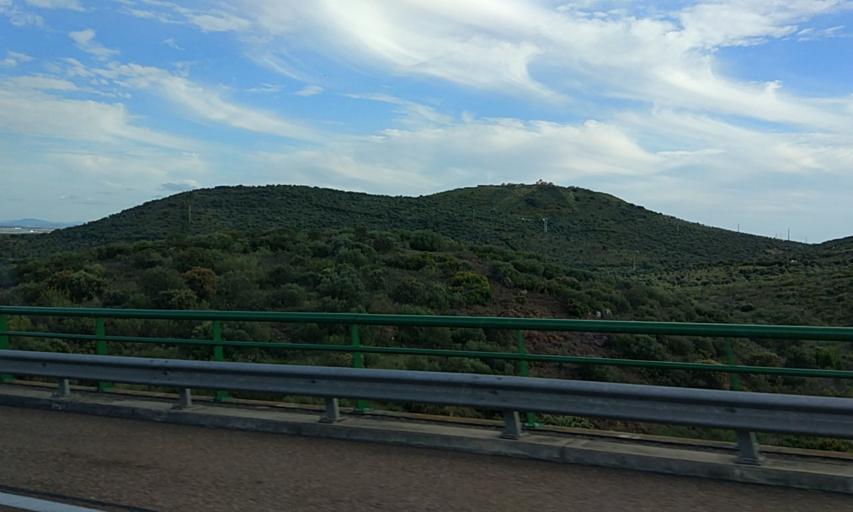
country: PT
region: Portalegre
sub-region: Elvas
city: Elvas
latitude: 38.9084
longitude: -7.1690
